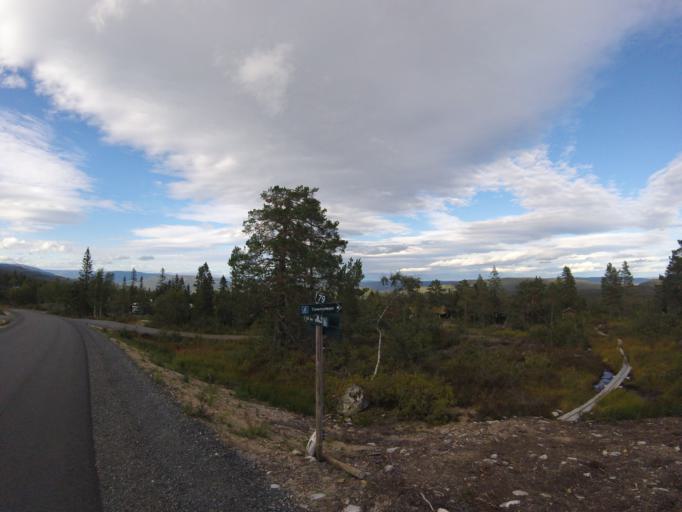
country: NO
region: Buskerud
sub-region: Flesberg
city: Lampeland
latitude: 59.7885
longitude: 9.4156
